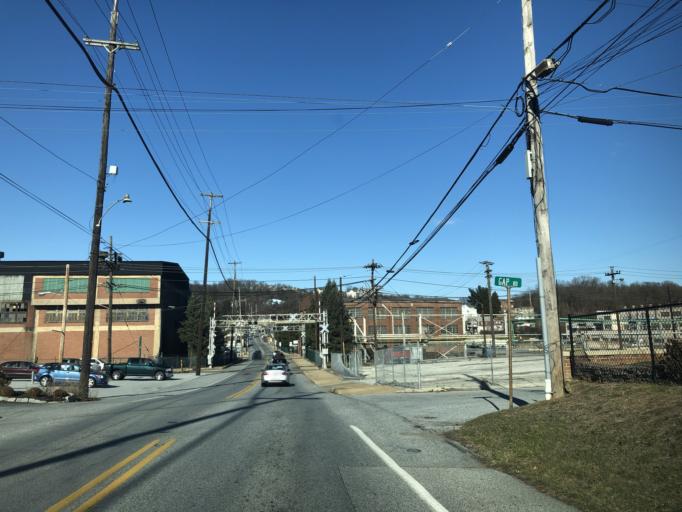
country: US
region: Pennsylvania
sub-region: Chester County
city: South Coatesville
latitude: 39.9757
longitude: -75.8286
